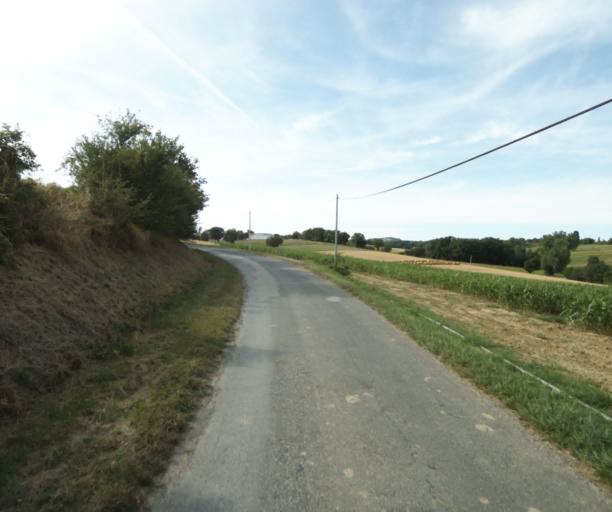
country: FR
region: Midi-Pyrenees
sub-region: Departement du Tarn
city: Puylaurens
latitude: 43.5303
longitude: 2.0590
